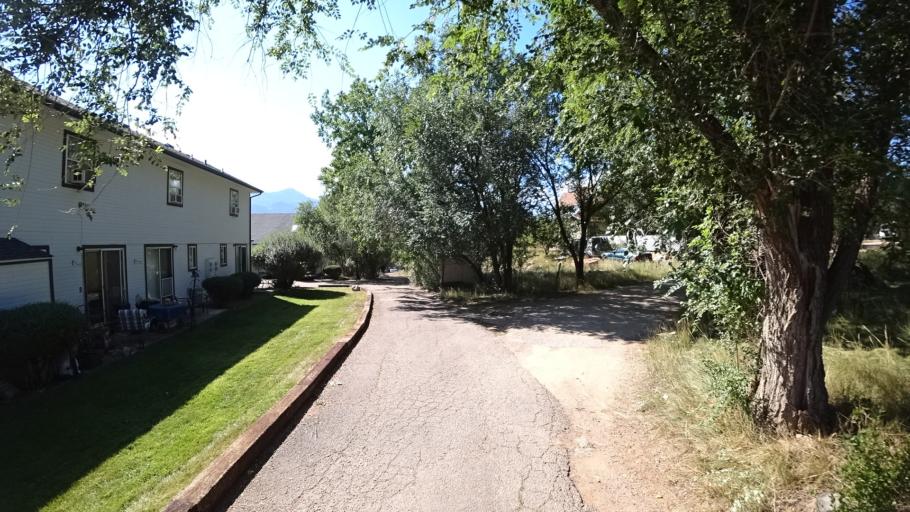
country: US
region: Colorado
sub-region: El Paso County
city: Colorado Springs
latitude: 38.8518
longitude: -104.8472
